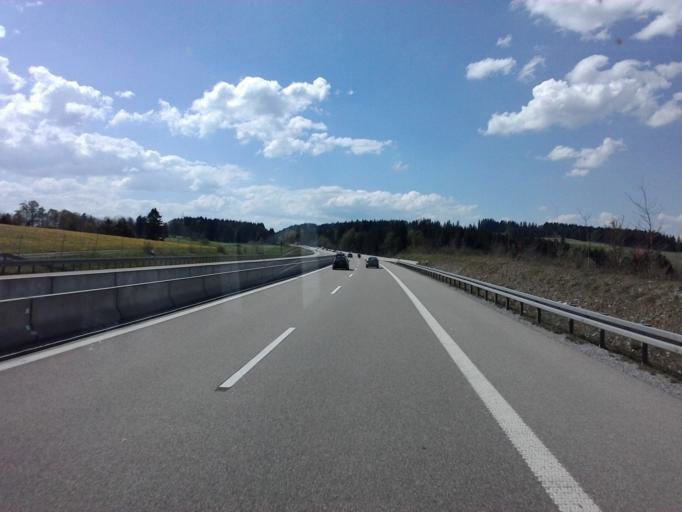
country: DE
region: Bavaria
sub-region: Swabia
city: Ruckholz
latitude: 47.6406
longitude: 10.5522
